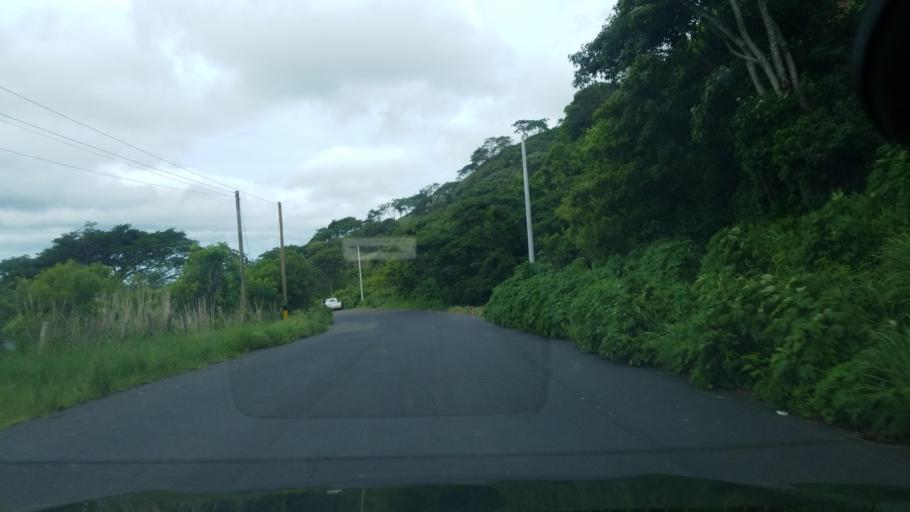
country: HN
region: Choluteca
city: Corpus
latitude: 13.3696
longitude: -86.9499
